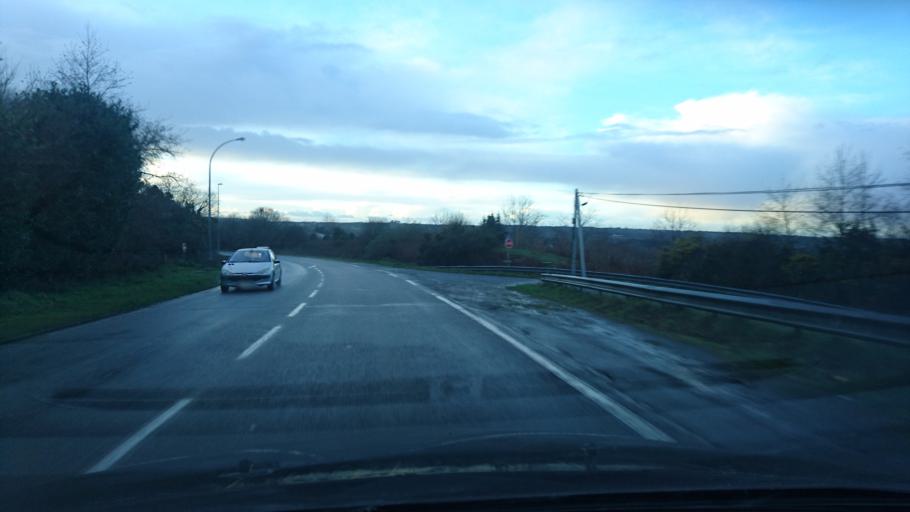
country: FR
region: Brittany
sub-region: Departement du Finistere
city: Guilers
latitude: 48.3895
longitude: -4.5323
